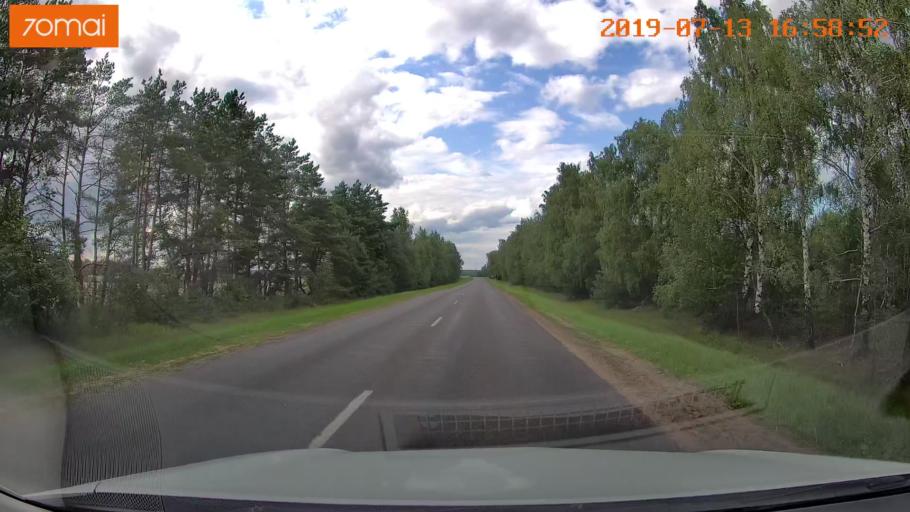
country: BY
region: Mogilev
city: Kirawsk
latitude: 53.2937
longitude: 29.4378
